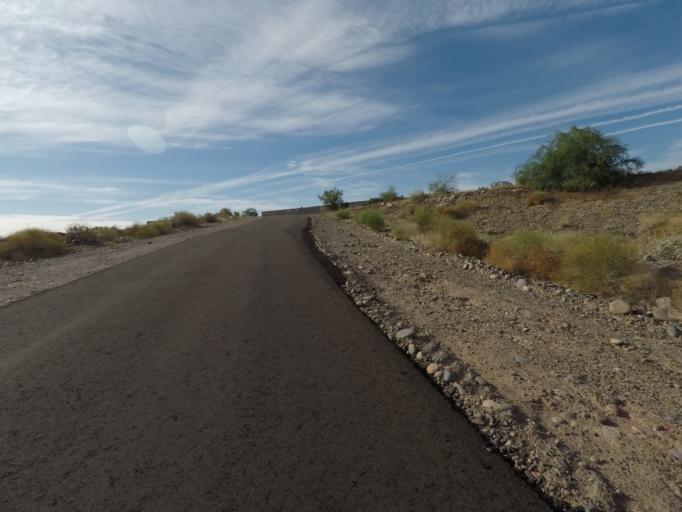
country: US
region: Arizona
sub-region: Maricopa County
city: Phoenix
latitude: 33.4158
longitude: -112.0271
